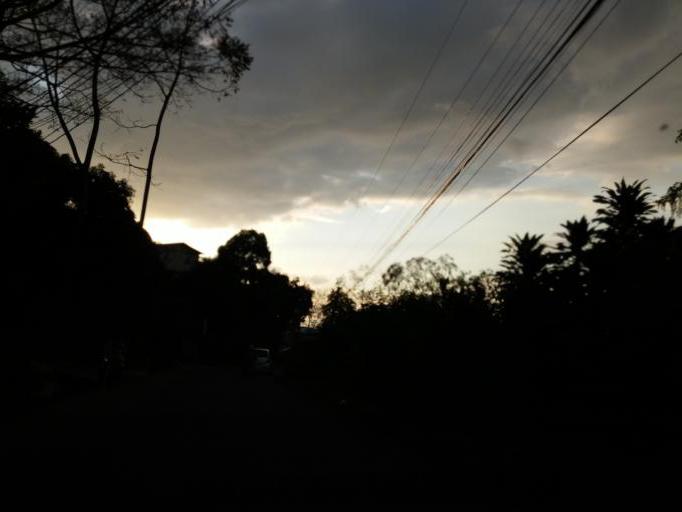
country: CR
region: San Jose
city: Palmichal
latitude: 9.8406
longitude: -84.2144
